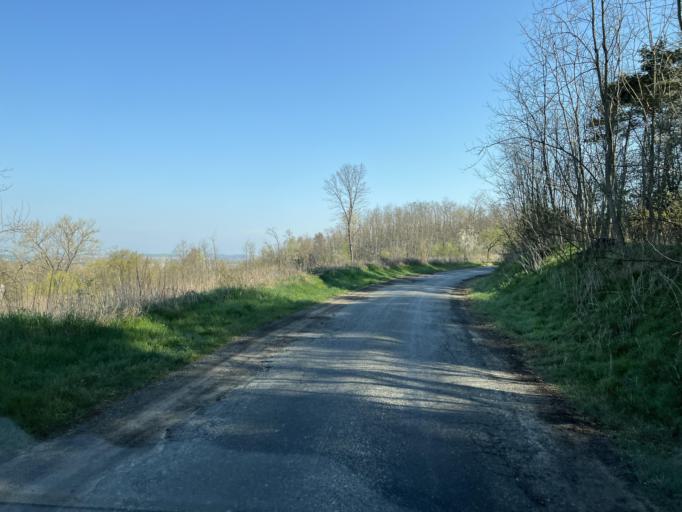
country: SK
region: Nitriansky
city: Sahy
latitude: 47.9958
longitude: 18.8185
